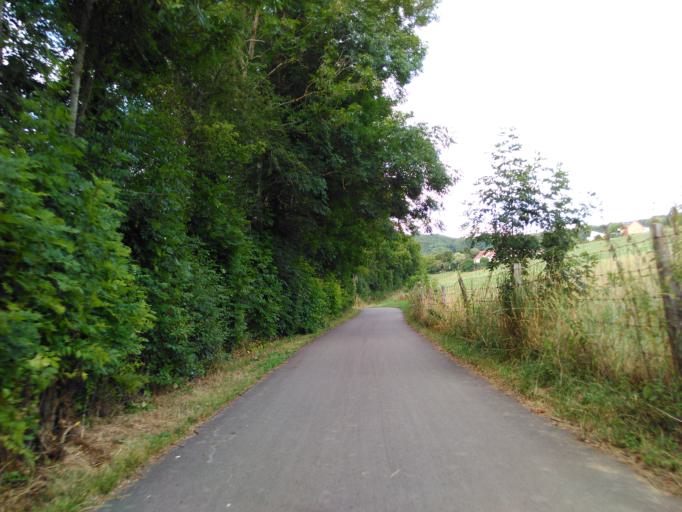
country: DE
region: Rheinland-Pfalz
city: Minden
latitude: 49.8182
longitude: 6.4638
